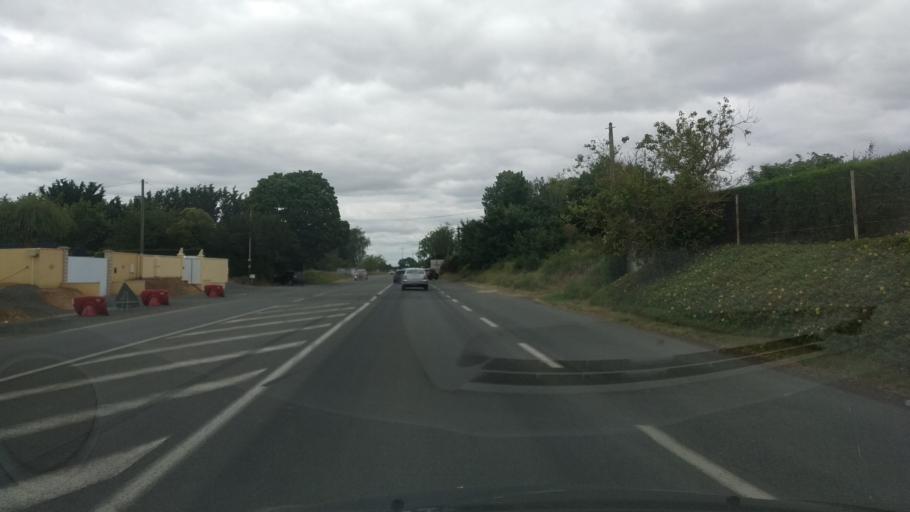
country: FR
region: Poitou-Charentes
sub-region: Departement de la Vienne
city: Migne-Auxances
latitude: 46.6031
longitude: 0.3124
